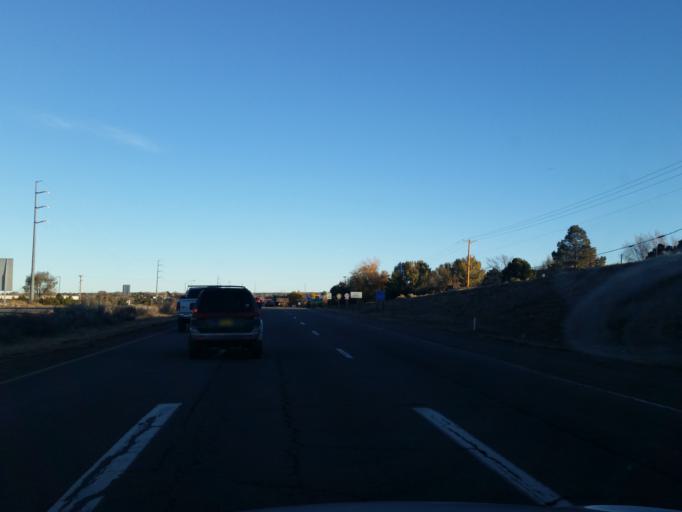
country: US
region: New Mexico
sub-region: Santa Fe County
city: Santa Fe
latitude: 35.6390
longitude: -105.9562
